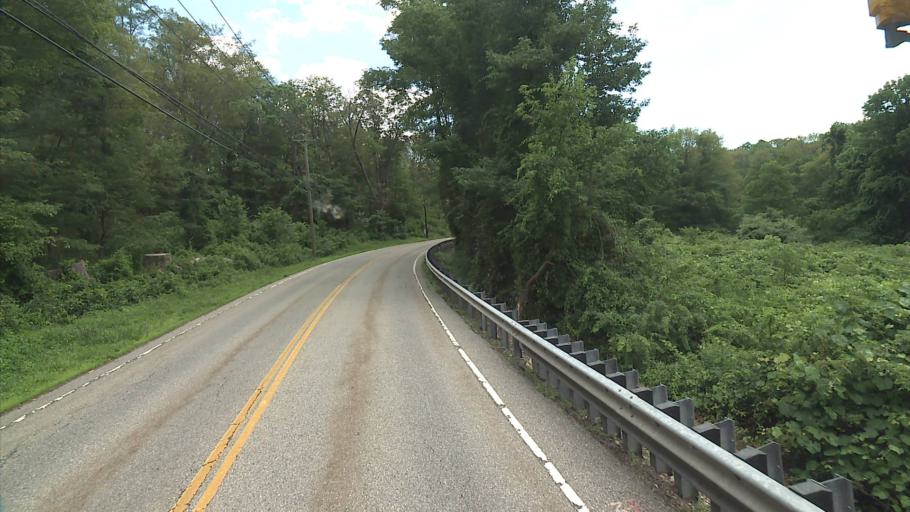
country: US
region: Connecticut
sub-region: Middlesex County
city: Higganum
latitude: 41.5315
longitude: -72.5387
